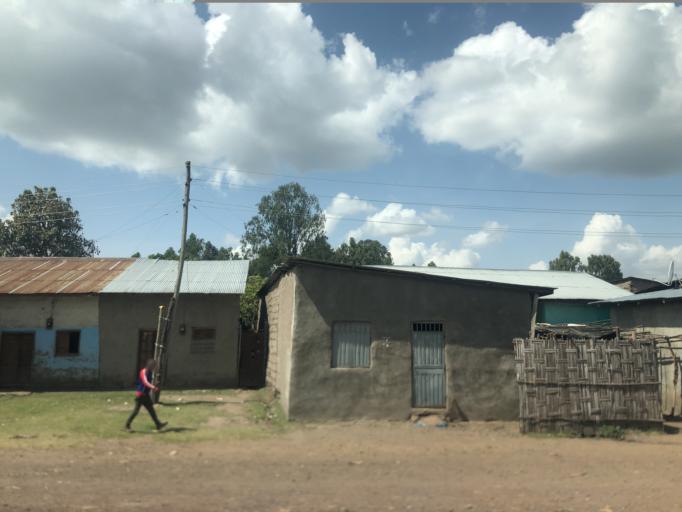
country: ET
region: Southern Nations, Nationalities, and People's Region
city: Boditi
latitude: 7.0326
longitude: 37.9192
